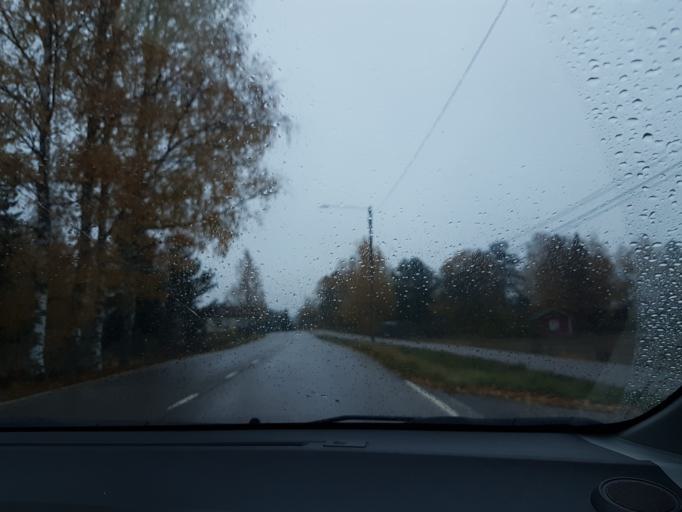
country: FI
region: Uusimaa
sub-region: Helsinki
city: Jaervenpaeae
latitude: 60.5697
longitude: 25.1467
